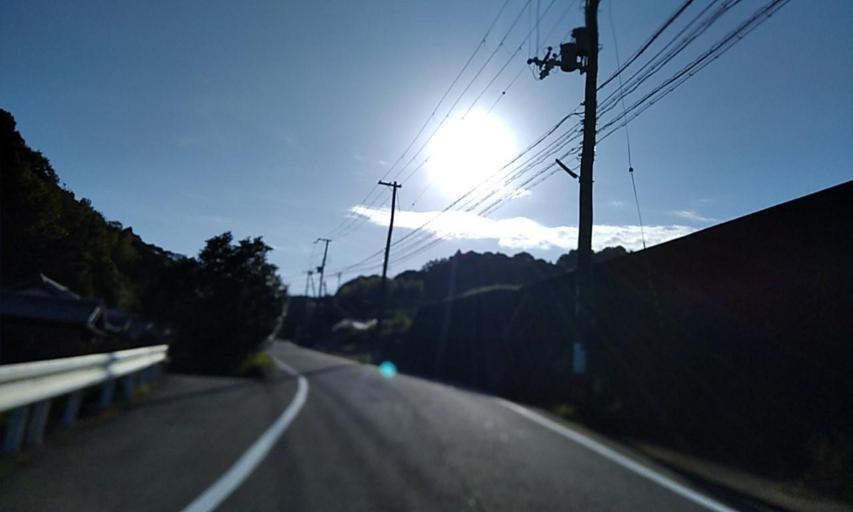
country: JP
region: Wakayama
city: Iwade
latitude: 34.1563
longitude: 135.2968
